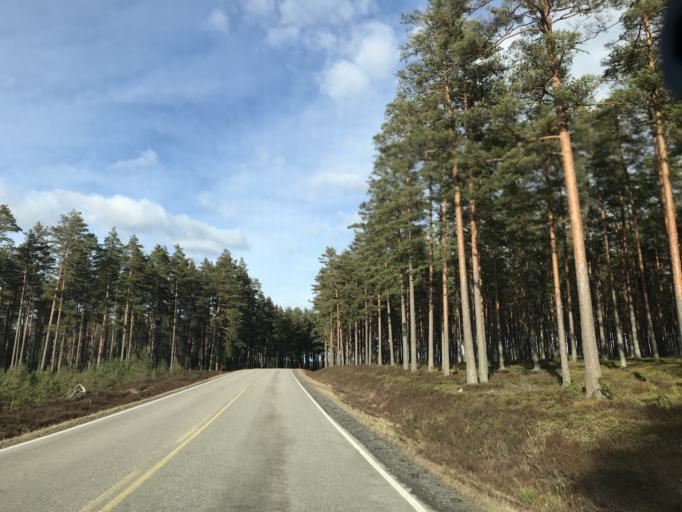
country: FI
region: Uusimaa
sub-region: Raaseporin
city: Ekenaes
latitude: 60.0707
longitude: 23.2881
